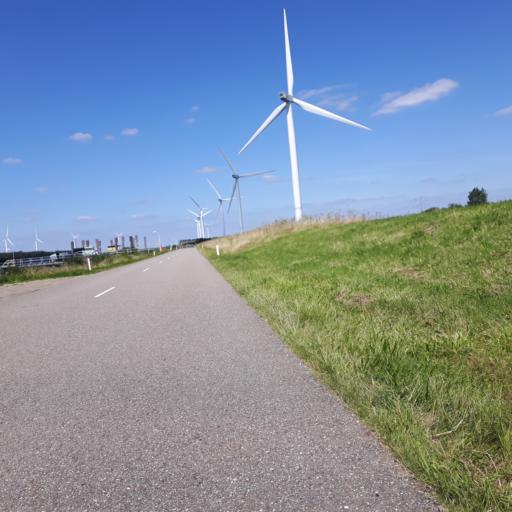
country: NL
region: North Brabant
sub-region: Gemeente Woensdrecht
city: Woensdrecht
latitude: 51.4365
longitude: 4.2355
